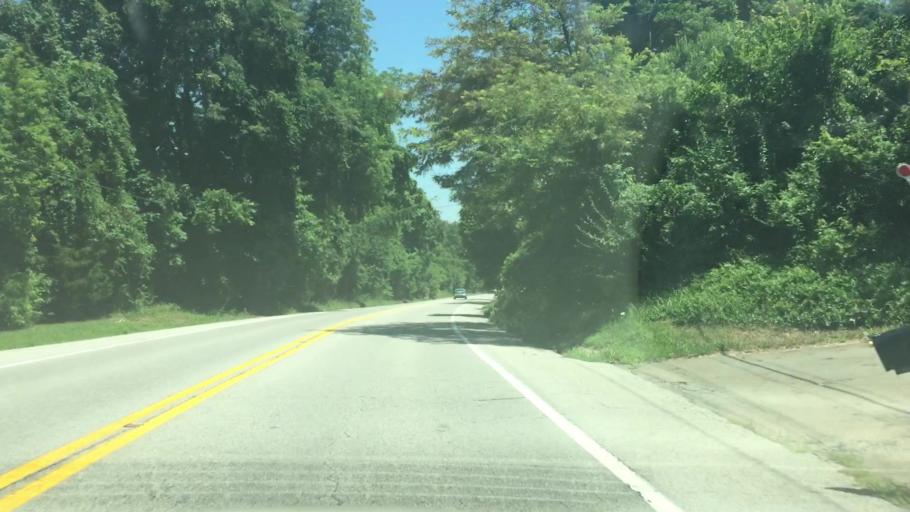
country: US
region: Maryland
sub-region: Cecil County
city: Rising Sun
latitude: 39.6819
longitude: -76.1505
